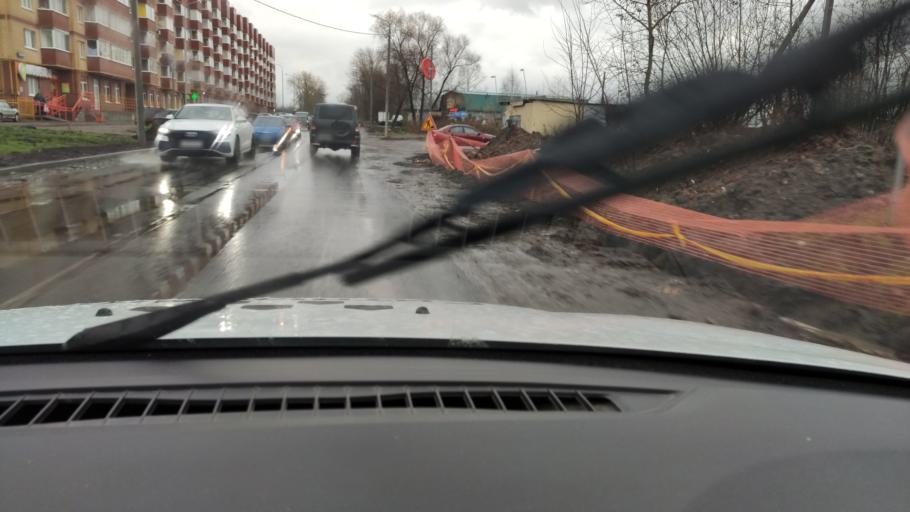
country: RU
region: Perm
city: Perm
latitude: 58.0349
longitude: 56.3599
